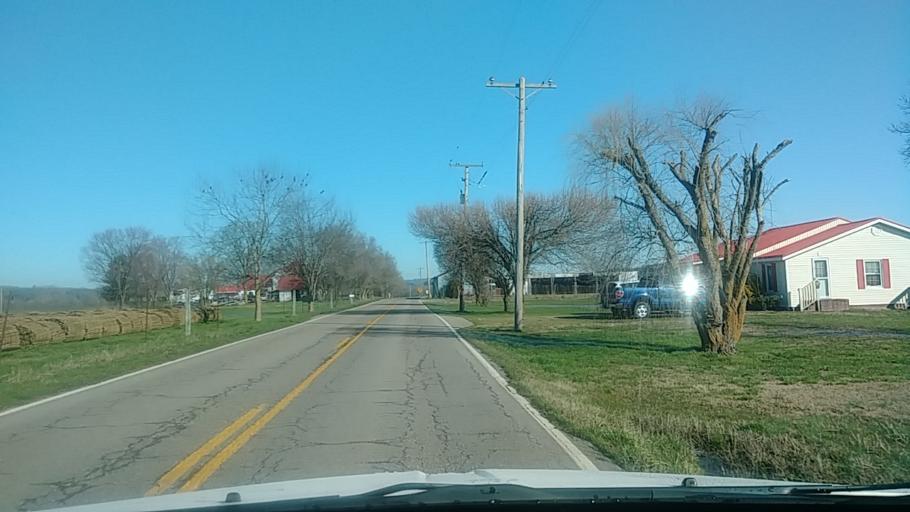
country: US
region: Tennessee
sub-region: Jefferson County
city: White Pine
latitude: 36.1610
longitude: -83.1624
